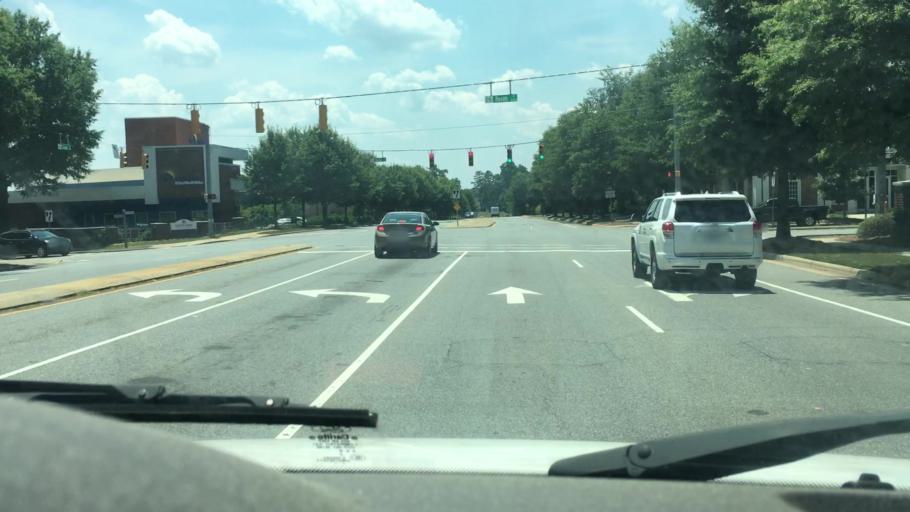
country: US
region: North Carolina
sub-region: Mecklenburg County
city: Huntersville
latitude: 35.4063
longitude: -80.8654
